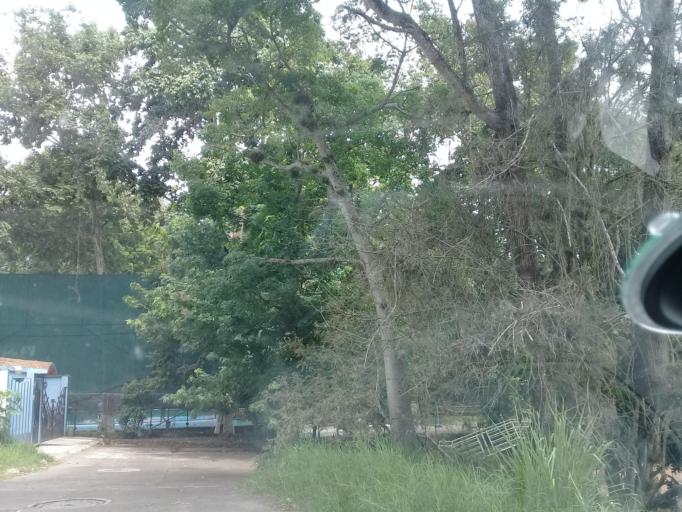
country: MX
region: Veracruz
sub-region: Xalapa
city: Colonia Santa Barbara
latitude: 19.5247
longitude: -96.8763
